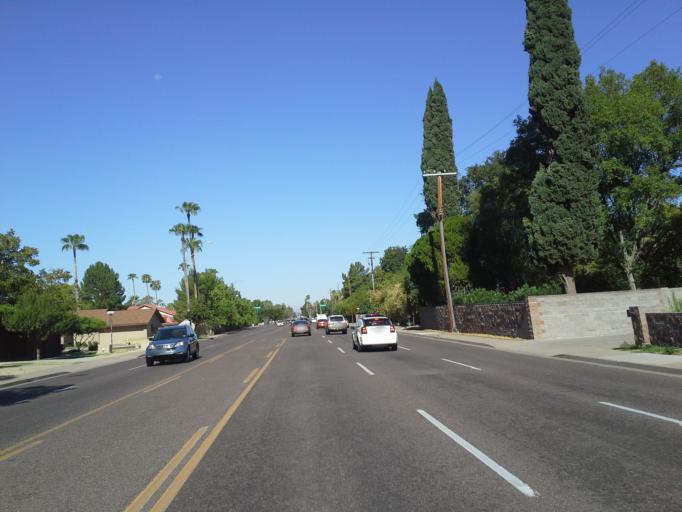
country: US
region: Arizona
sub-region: Maricopa County
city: Phoenix
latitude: 33.5529
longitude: -112.0796
